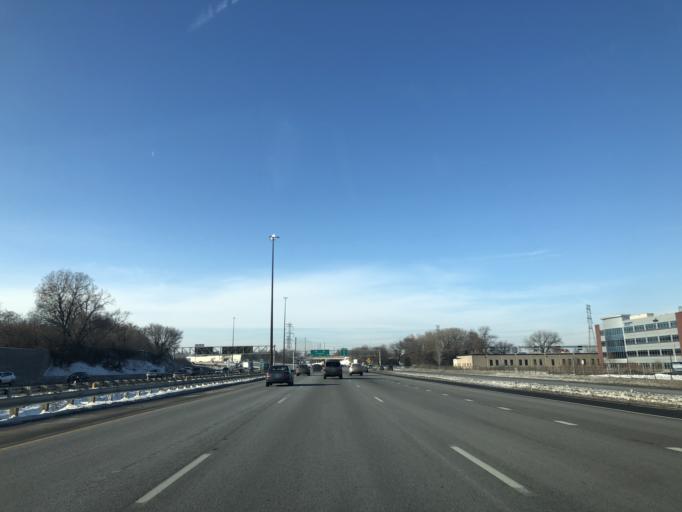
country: US
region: Minnesota
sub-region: Ramsey County
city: Lauderdale
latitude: 45.0114
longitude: -93.1972
